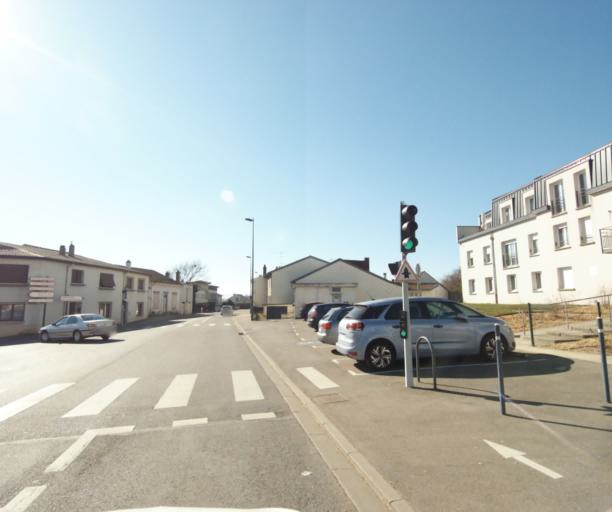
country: FR
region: Lorraine
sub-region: Departement de Meurthe-et-Moselle
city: Saulxures-les-Nancy
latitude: 48.6875
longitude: 6.2449
